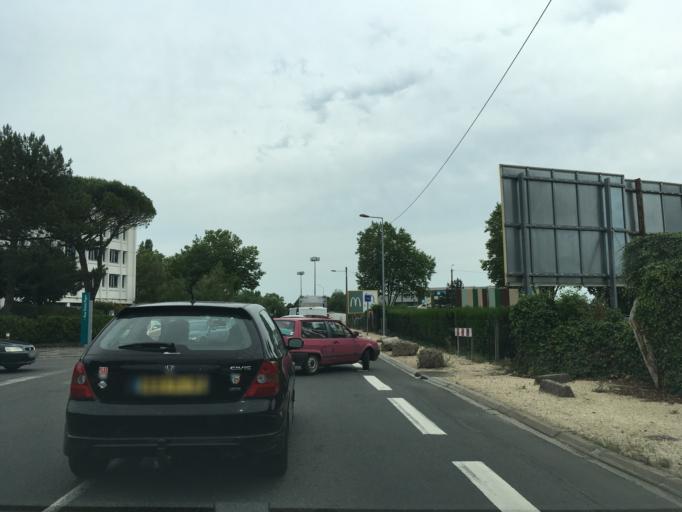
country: FR
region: Poitou-Charentes
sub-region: Departement des Deux-Sevres
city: Niort
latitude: 46.3100
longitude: -0.4835
